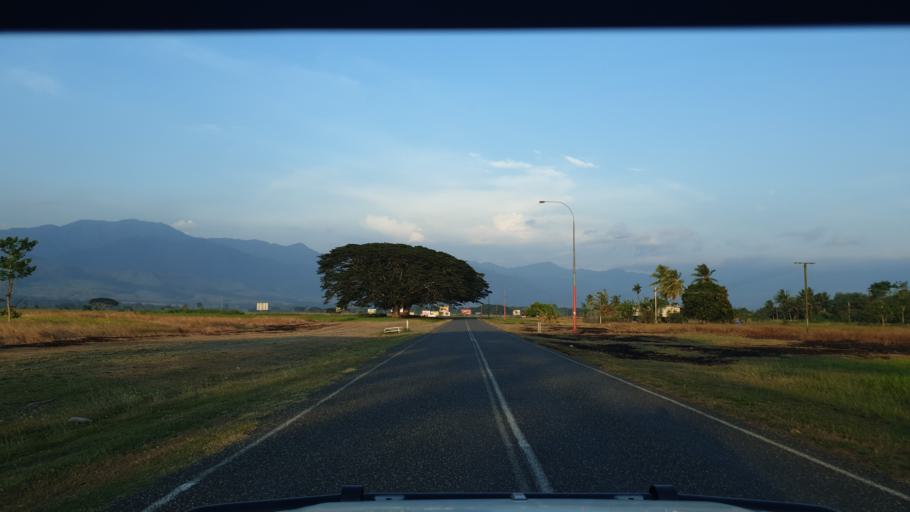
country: PG
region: Morobe
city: Lae
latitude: -6.5660
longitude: 146.7435
